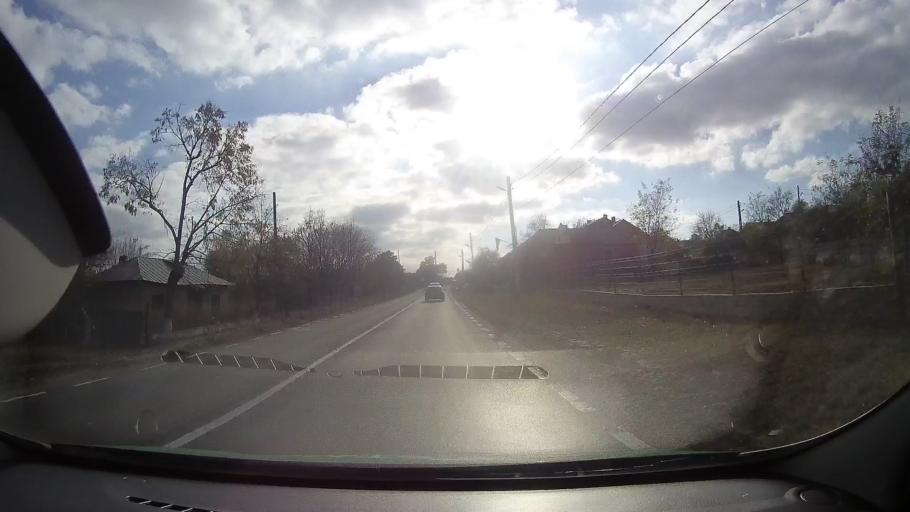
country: RO
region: Tulcea
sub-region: Comuna Topolog
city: Topolog
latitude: 44.8750
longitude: 28.3737
